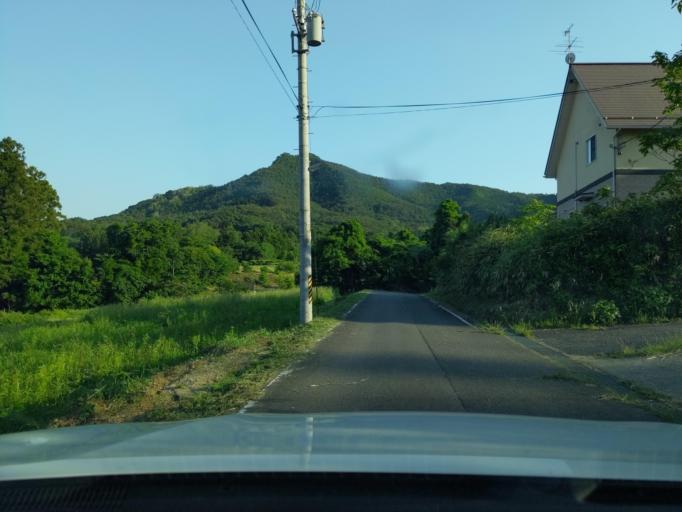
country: JP
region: Fukushima
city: Motomiya
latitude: 37.5258
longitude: 140.3550
